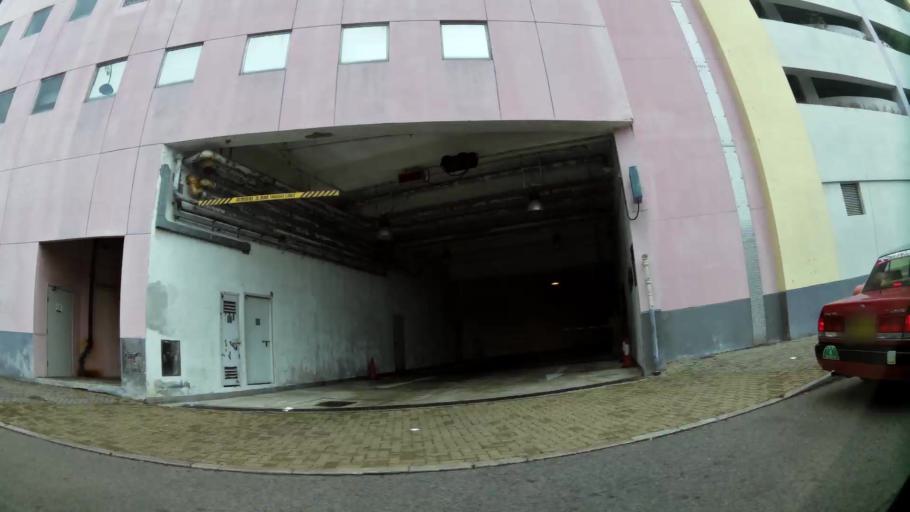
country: HK
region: Wanchai
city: Wan Chai
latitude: 22.2427
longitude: 114.1651
